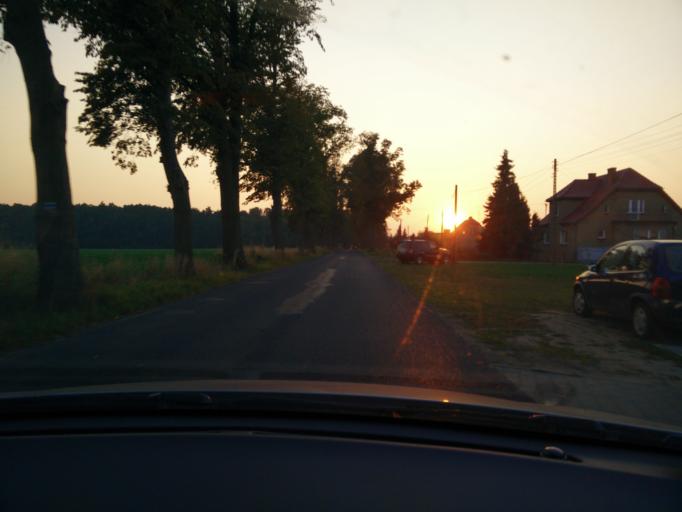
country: PL
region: Greater Poland Voivodeship
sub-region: Powiat wrzesinski
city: Miloslaw
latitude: 52.2058
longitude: 17.4712
